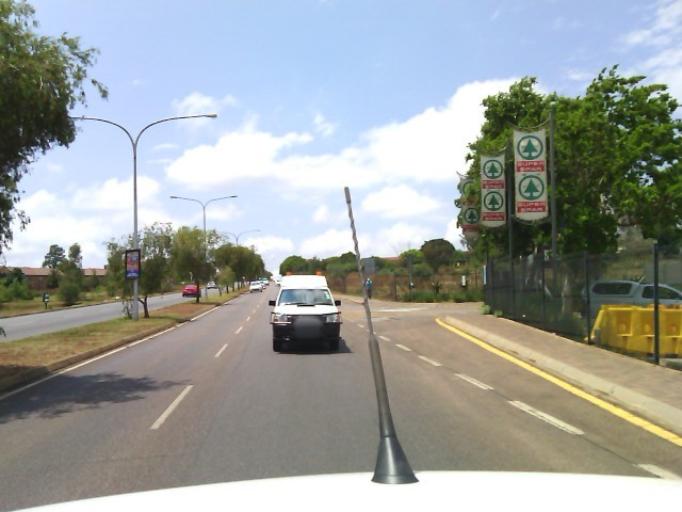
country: ZA
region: Gauteng
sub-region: City of Tshwane Metropolitan Municipality
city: Centurion
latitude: -25.8368
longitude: 28.1922
